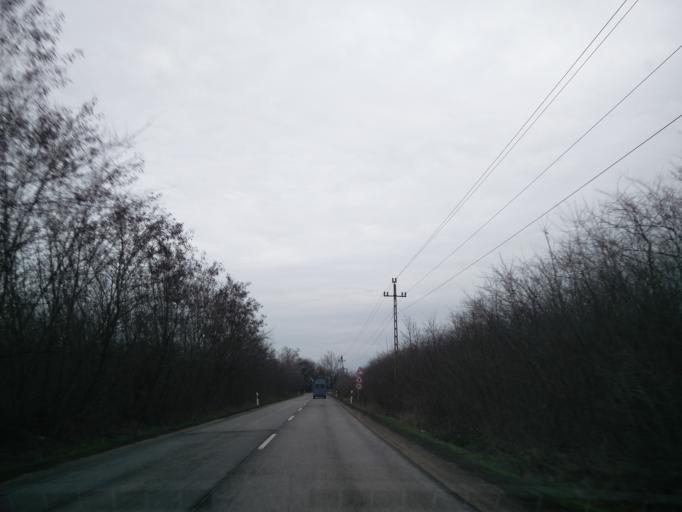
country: HU
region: Pest
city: Ullo
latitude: 47.4022
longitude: 19.3752
